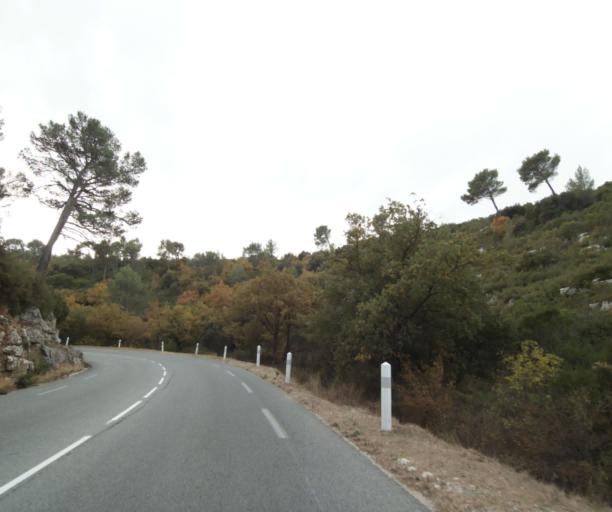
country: FR
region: Provence-Alpes-Cote d'Azur
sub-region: Departement des Bouches-du-Rhone
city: Cuges-les-Pins
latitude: 43.2662
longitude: 5.6618
